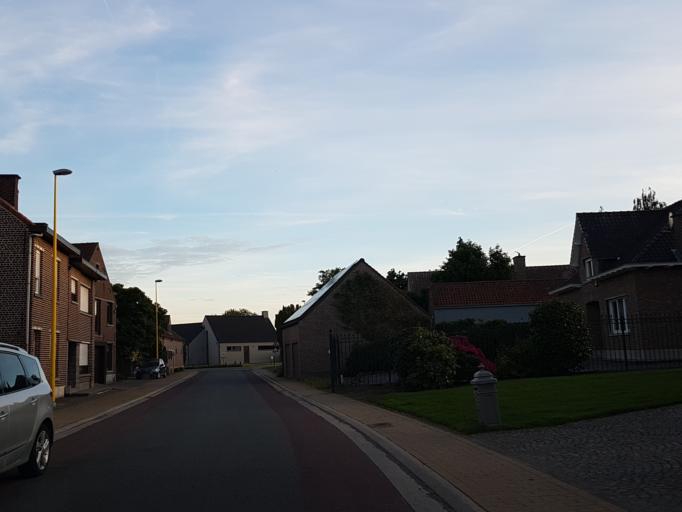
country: BE
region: Flanders
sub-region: Provincie Vlaams-Brabant
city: Meise
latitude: 50.9593
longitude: 4.2879
